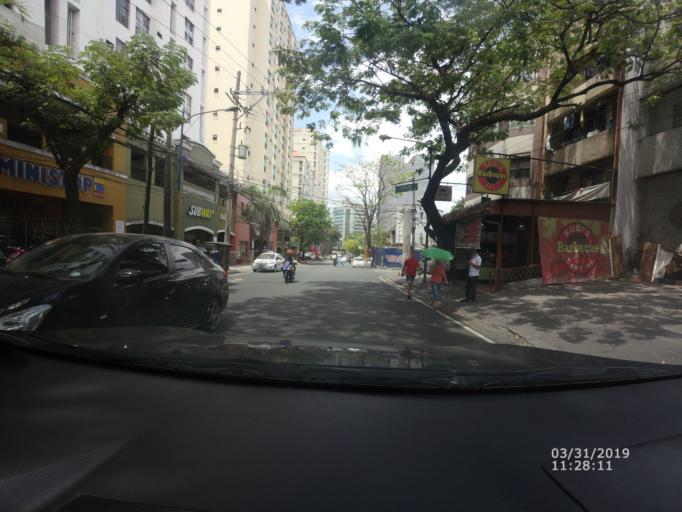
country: PH
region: Metro Manila
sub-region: Mandaluyong
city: Mandaluyong City
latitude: 14.5793
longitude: 121.0479
